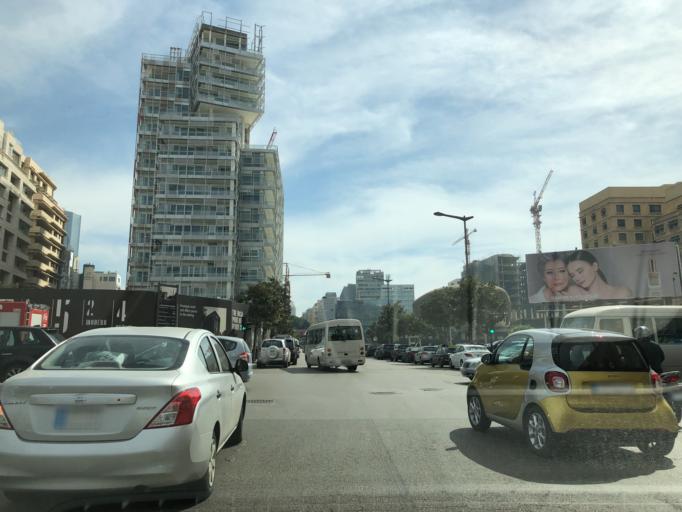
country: LB
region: Beyrouth
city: Beirut
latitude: 33.8951
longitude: 35.5065
